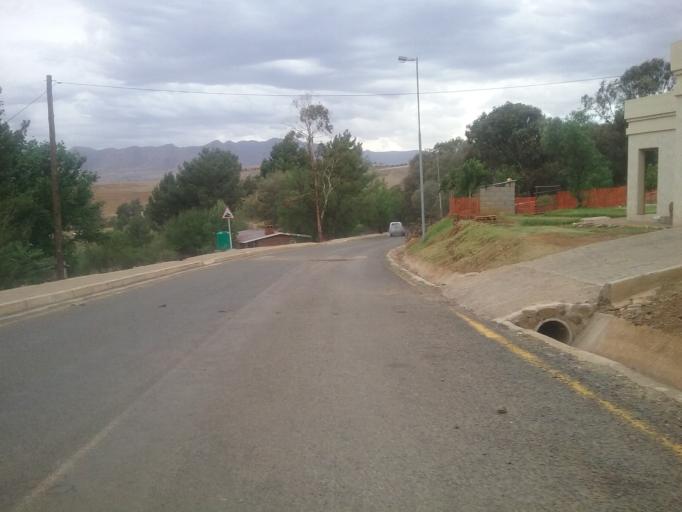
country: LS
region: Quthing
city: Quthing
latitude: -30.4112
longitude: 27.7104
